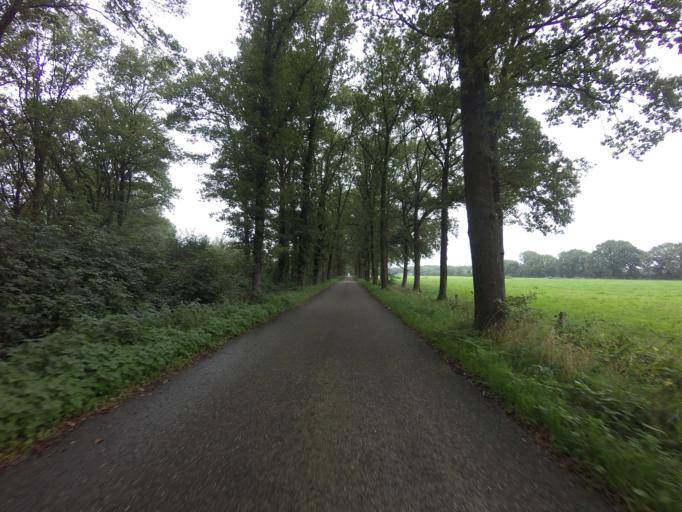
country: NL
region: Overijssel
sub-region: Gemeente Enschede
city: Enschede
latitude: 52.1899
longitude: 6.9287
